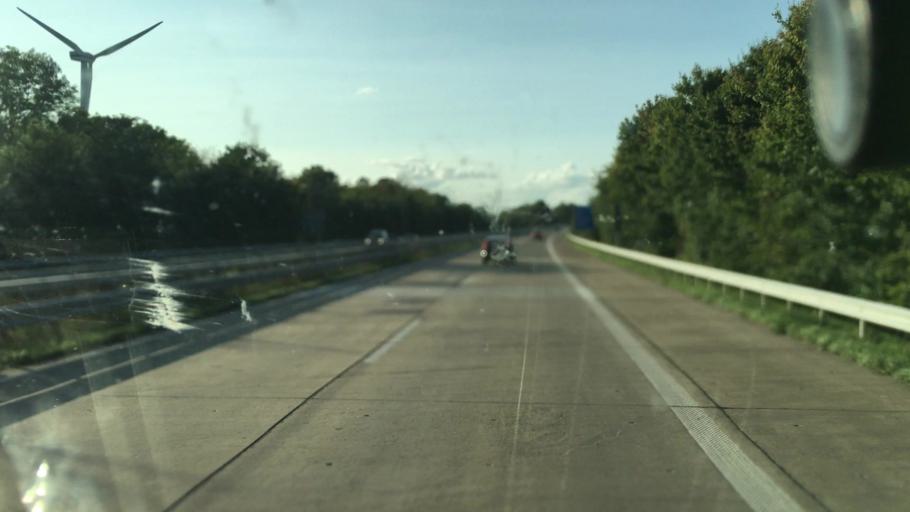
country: DE
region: Lower Saxony
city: Bockhorn
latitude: 53.4386
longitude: 8.0363
